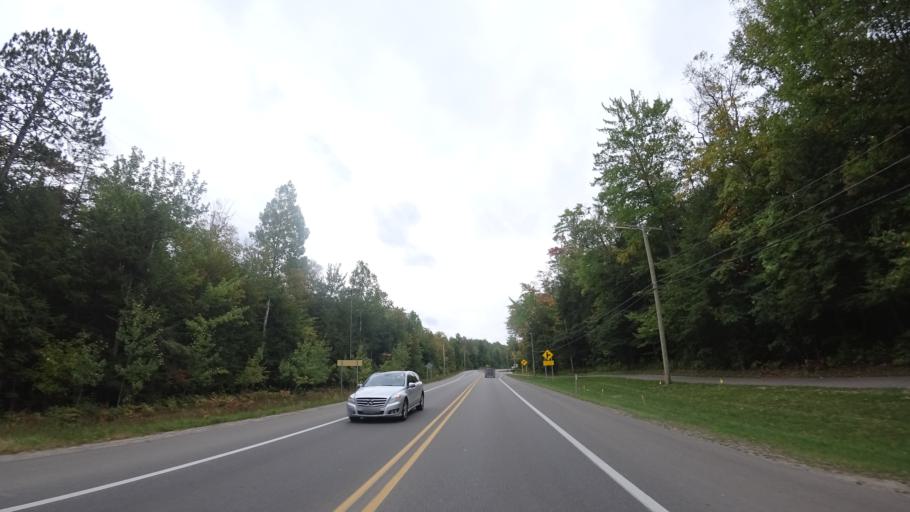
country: US
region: Michigan
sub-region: Emmet County
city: Petoskey
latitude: 45.4121
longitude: -84.9036
